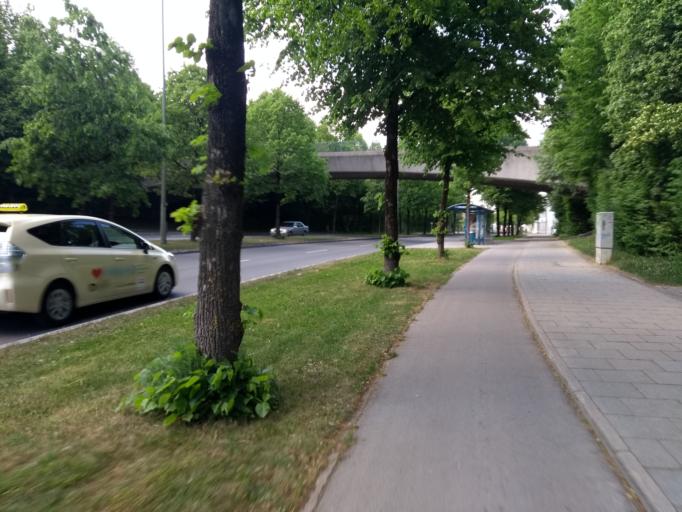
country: DE
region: Bavaria
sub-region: Upper Bavaria
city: Munich
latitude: 48.1263
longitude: 11.5361
